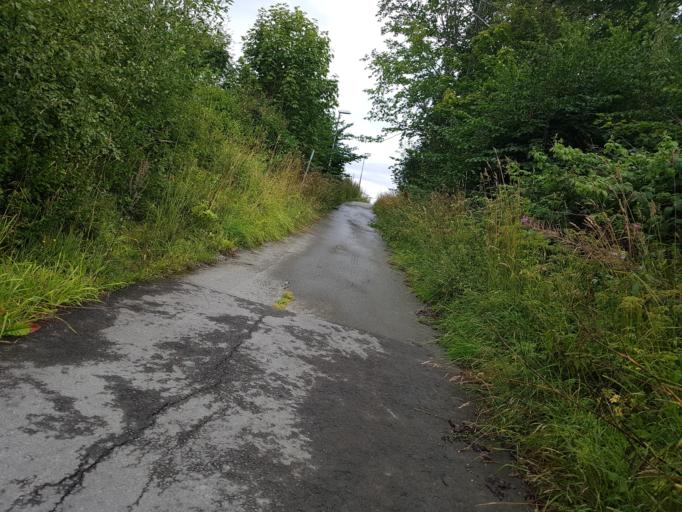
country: NO
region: Sor-Trondelag
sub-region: Trondheim
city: Trondheim
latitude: 63.3986
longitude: 10.4190
